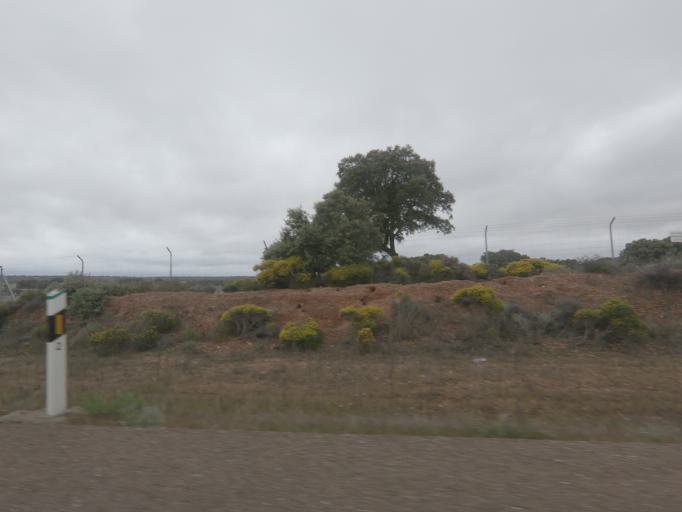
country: ES
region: Extremadura
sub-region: Provincia de Badajoz
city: Villar del Rey
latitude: 39.0259
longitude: -6.8419
